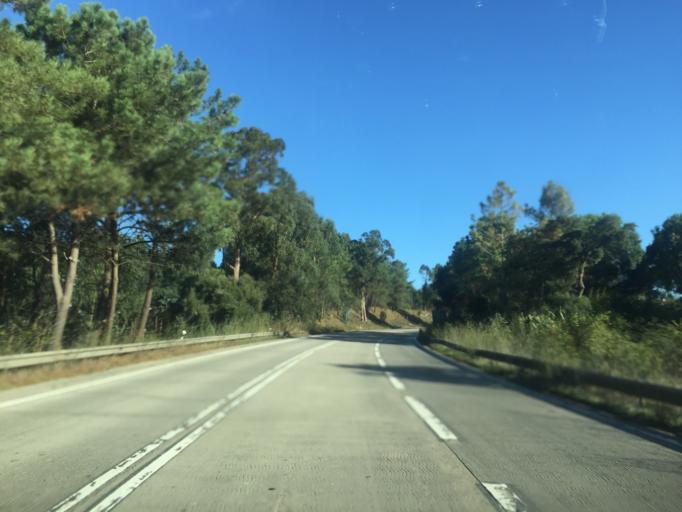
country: PT
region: Santarem
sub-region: Rio Maior
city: Rio Maior
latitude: 39.3001
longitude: -8.9481
